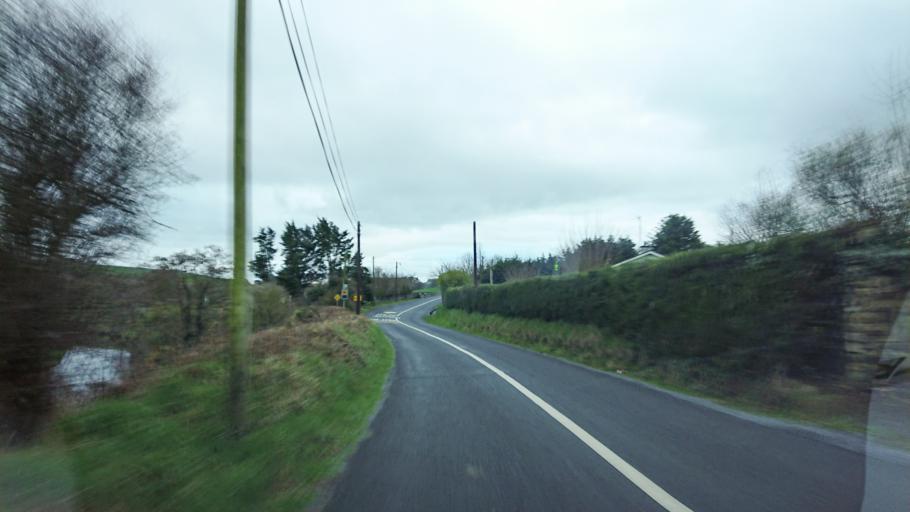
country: IE
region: Munster
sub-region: Waterford
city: Portlaw
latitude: 52.1565
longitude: -7.3838
